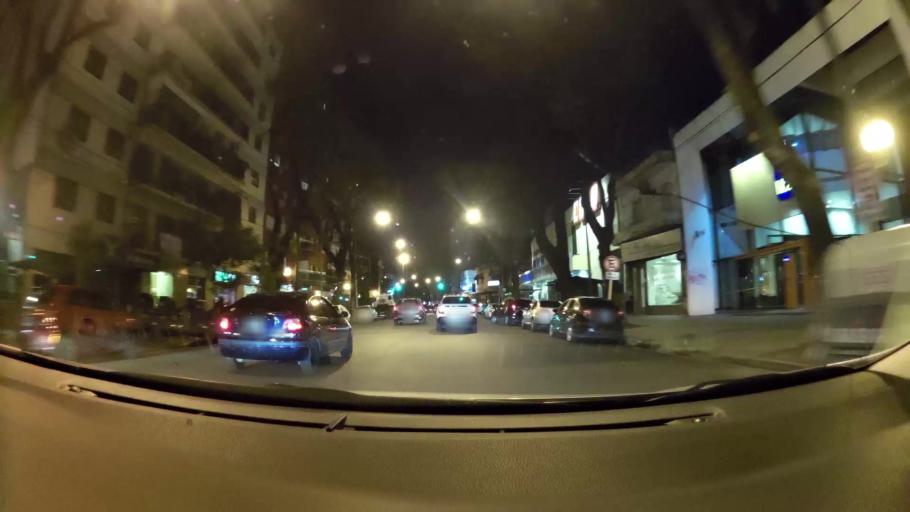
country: AR
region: Buenos Aires F.D.
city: Colegiales
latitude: -34.5715
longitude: -58.4585
